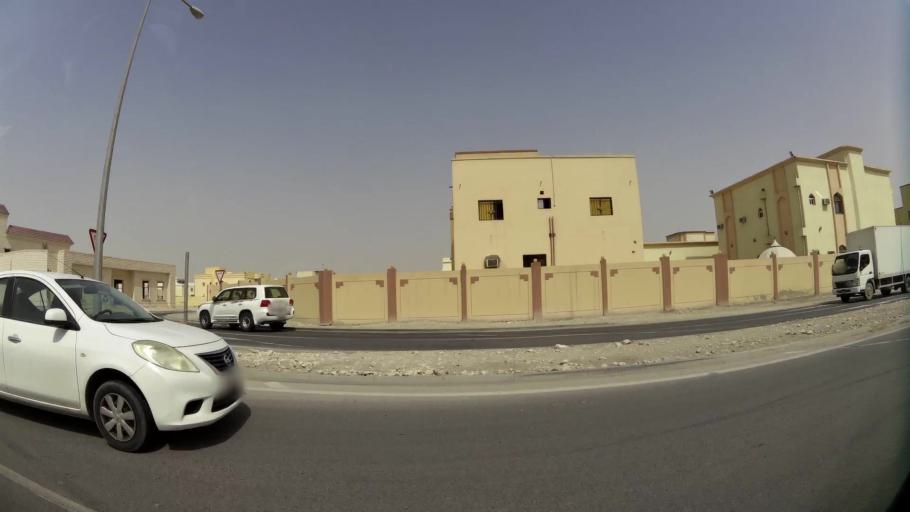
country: QA
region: Baladiyat ar Rayyan
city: Ar Rayyan
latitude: 25.2344
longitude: 51.3830
